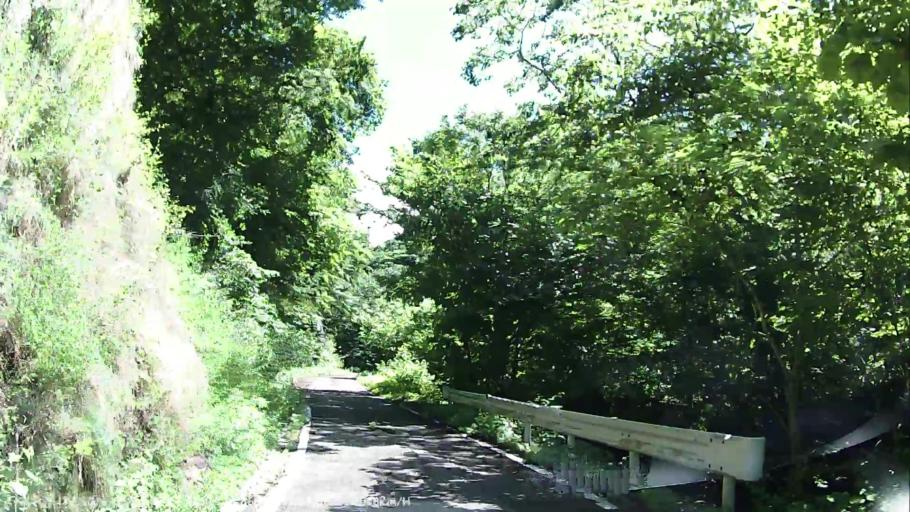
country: JP
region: Fukushima
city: Kitakata
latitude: 37.3675
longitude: 139.8608
